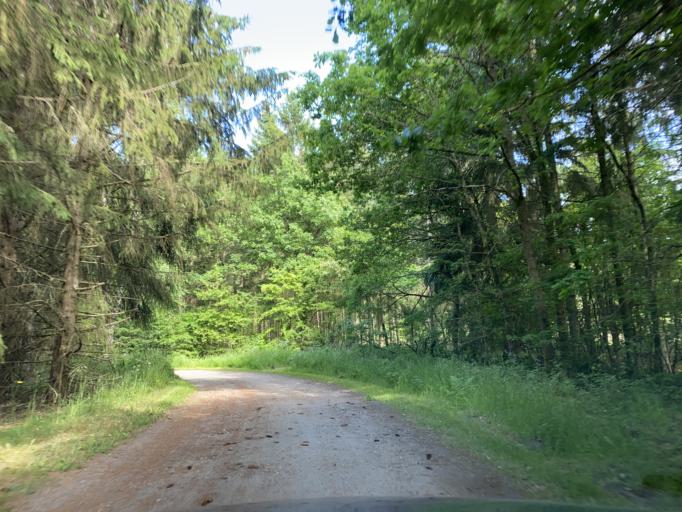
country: DK
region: Central Jutland
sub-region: Silkeborg Kommune
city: Svejbaek
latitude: 56.2356
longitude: 9.6825
